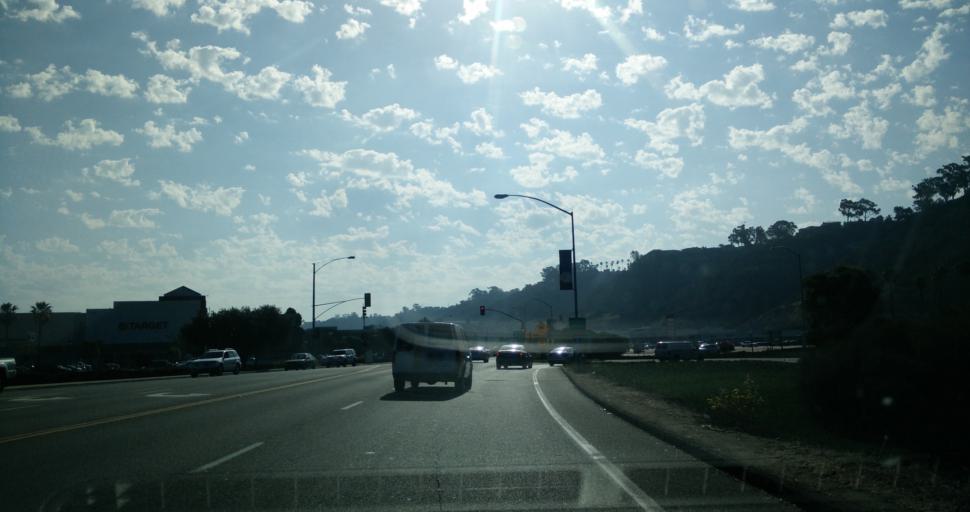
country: US
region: California
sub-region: San Diego County
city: San Diego
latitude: 32.7669
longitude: -117.1529
